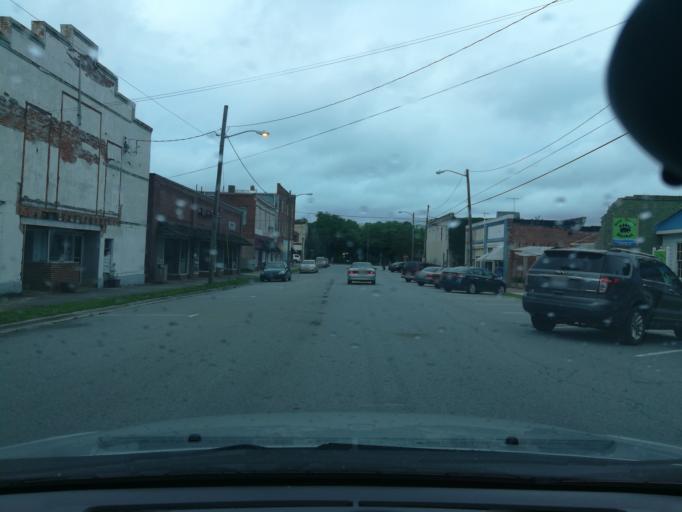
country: US
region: North Carolina
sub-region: Washington County
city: Plymouth
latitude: 35.8664
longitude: -76.7505
